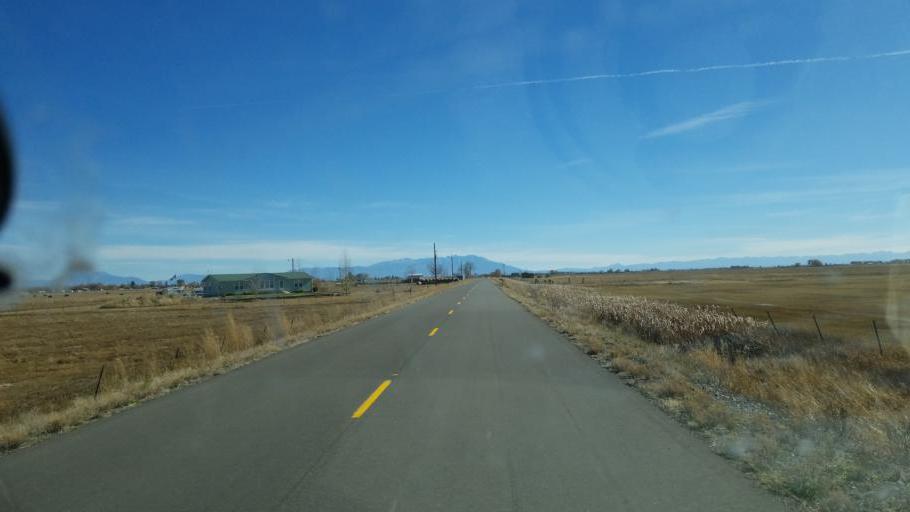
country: US
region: Colorado
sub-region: Rio Grande County
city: Monte Vista
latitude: 37.5604
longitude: -106.1699
